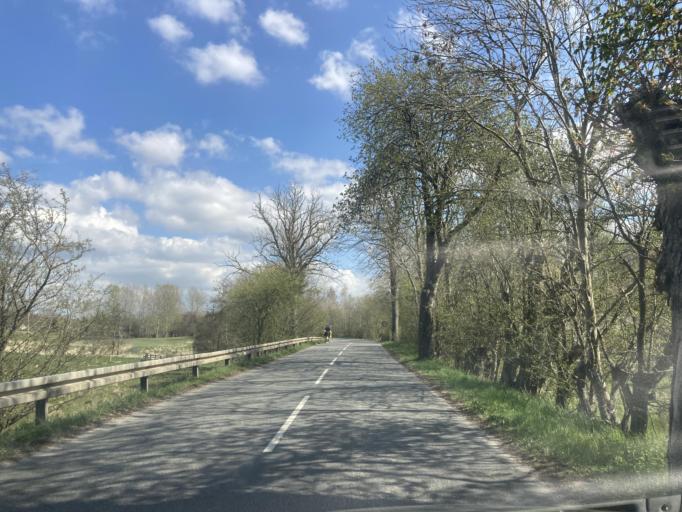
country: DK
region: Capital Region
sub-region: Gribskov Kommune
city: Helsinge
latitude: 55.9956
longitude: 12.2248
